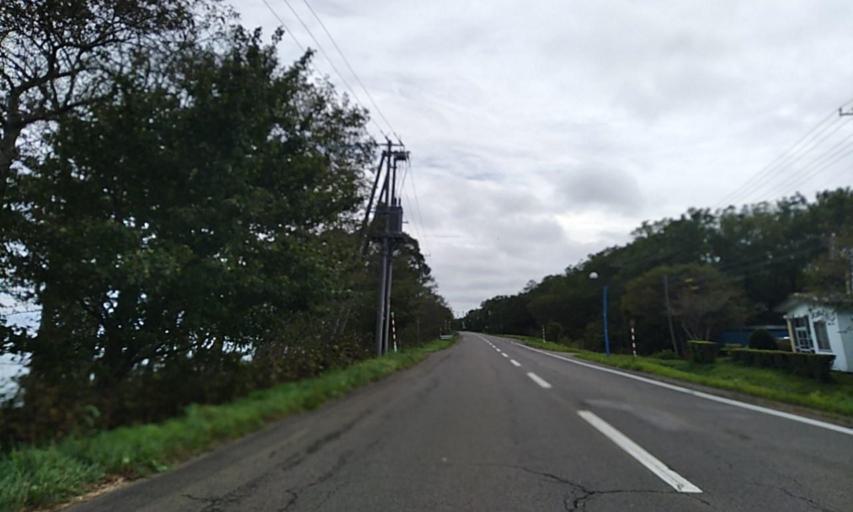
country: JP
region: Hokkaido
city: Shibetsu
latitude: 43.5970
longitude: 145.1978
